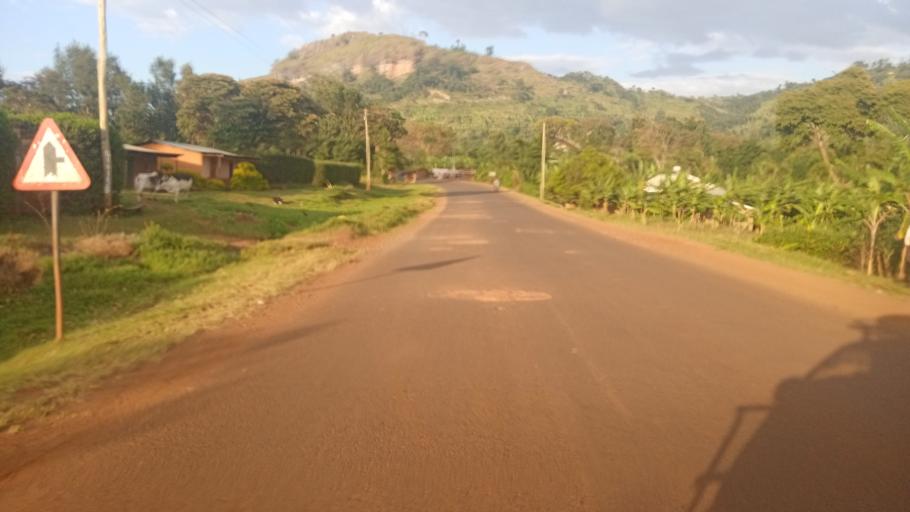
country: UG
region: Eastern Region
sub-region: Kapchorwa District
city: Kapchorwa
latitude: 1.3259
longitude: 34.3551
